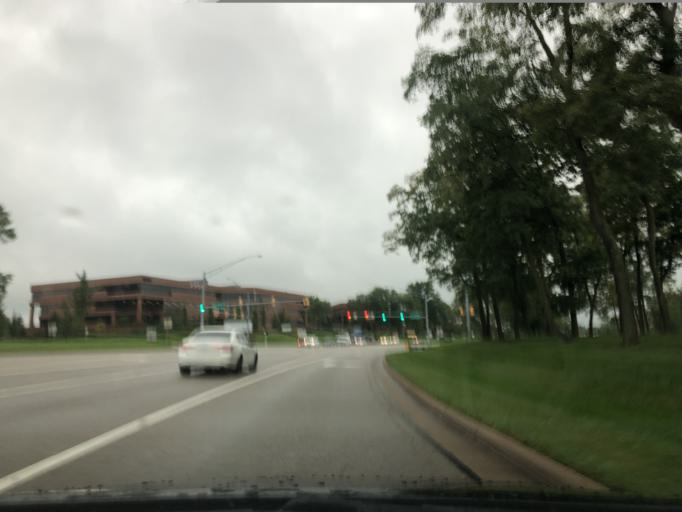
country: US
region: Ohio
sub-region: Hamilton County
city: Blue Ash
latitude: 39.2467
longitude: -84.3809
